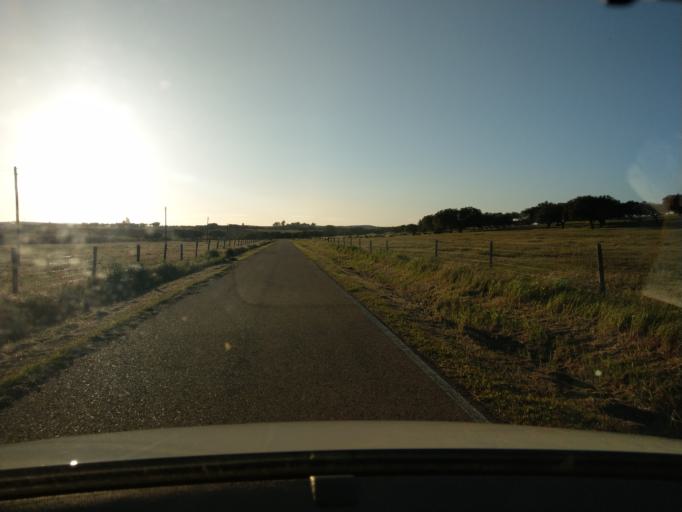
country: PT
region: Portalegre
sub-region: Campo Maior
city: Campo Maior
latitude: 39.1012
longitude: -7.0584
